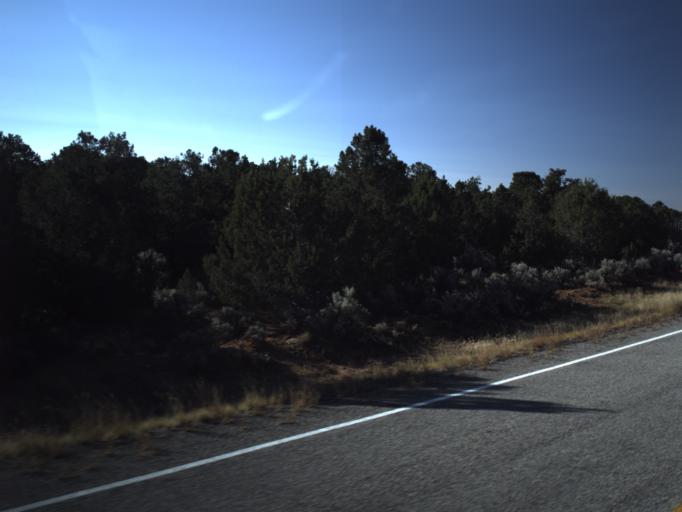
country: US
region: Utah
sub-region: San Juan County
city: Blanding
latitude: 37.5797
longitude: -109.9176
